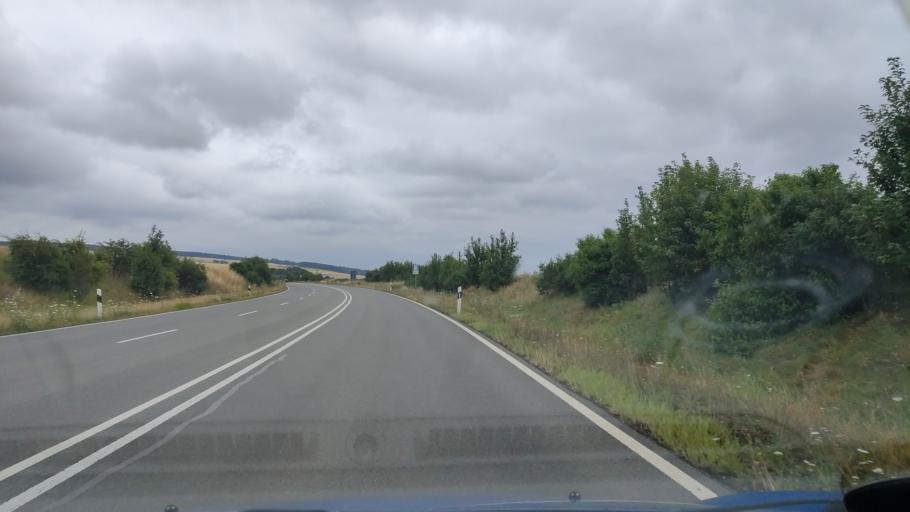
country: DE
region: Lower Saxony
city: Bad Munder am Deister
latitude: 52.2252
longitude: 9.4206
